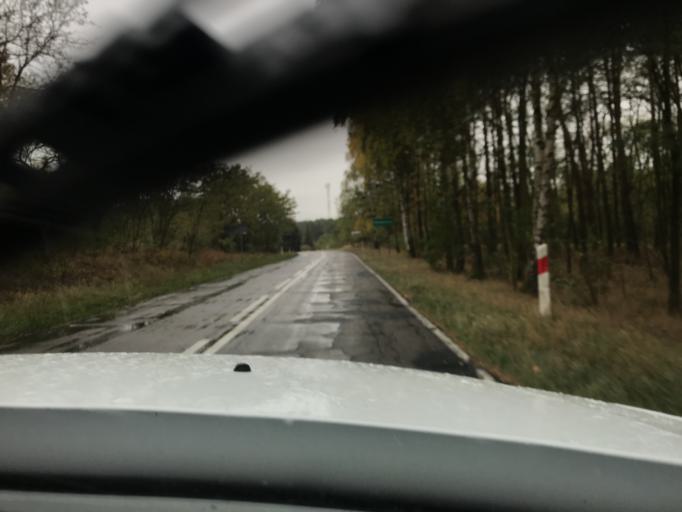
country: DE
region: Brandenburg
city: Neulewin
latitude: 52.7693
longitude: 14.3145
